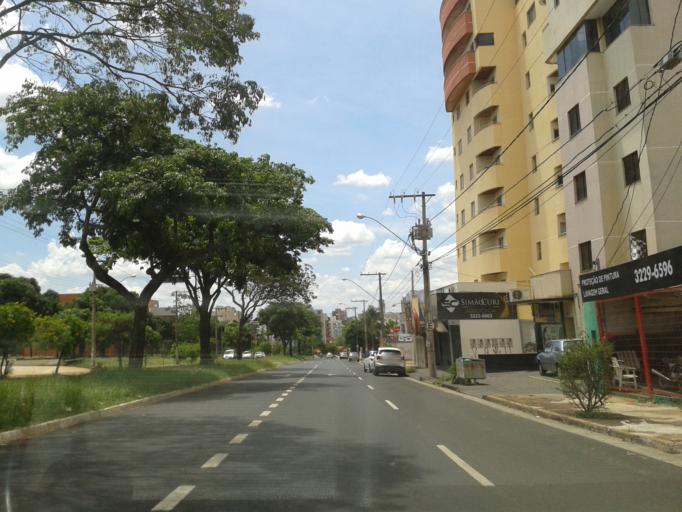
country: BR
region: Minas Gerais
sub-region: Uberlandia
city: Uberlandia
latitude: -18.9165
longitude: -48.2560
